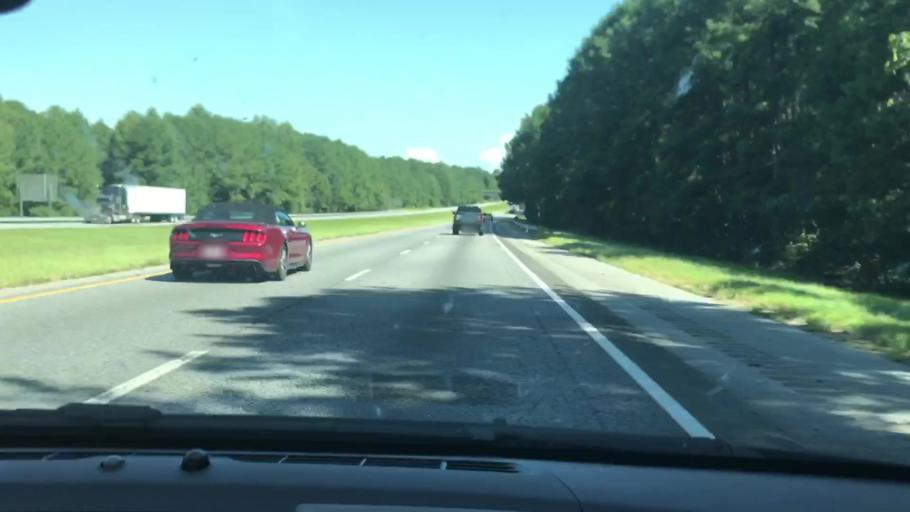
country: US
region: Alabama
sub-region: Russell County
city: Phenix City
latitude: 32.5774
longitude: -84.9614
